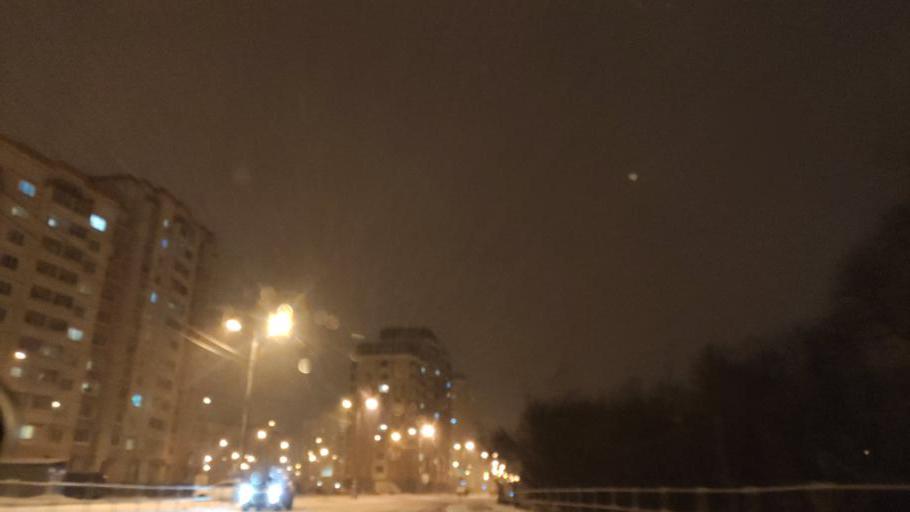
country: RU
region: Moskovskaya
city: Shcherbinka
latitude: 55.5414
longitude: 37.5645
